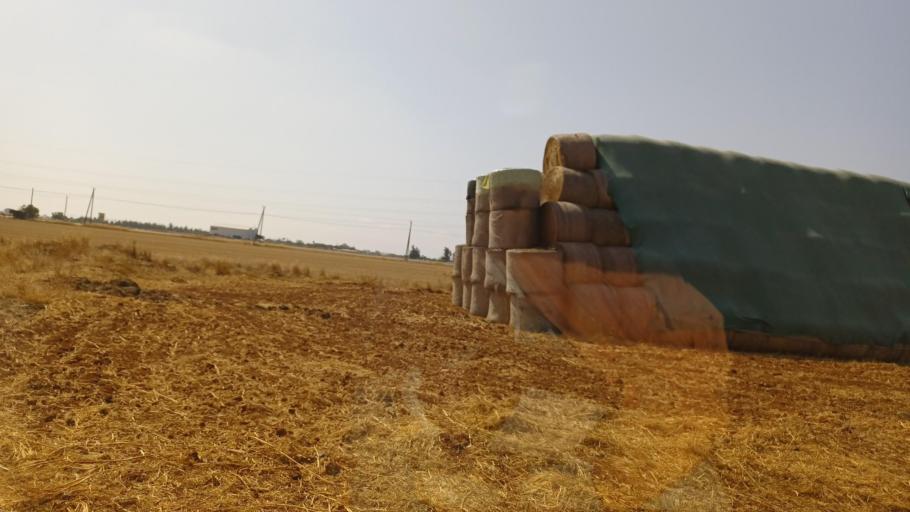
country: CY
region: Ammochostos
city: Avgorou
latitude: 35.0178
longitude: 33.8220
